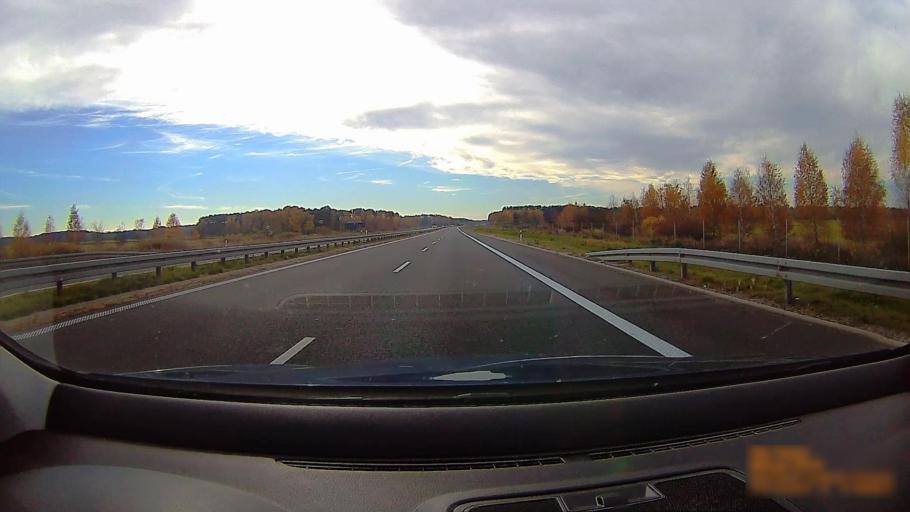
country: PL
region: Greater Poland Voivodeship
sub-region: Powiat ostrowski
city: Przygodzice
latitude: 51.5769
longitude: 17.8491
